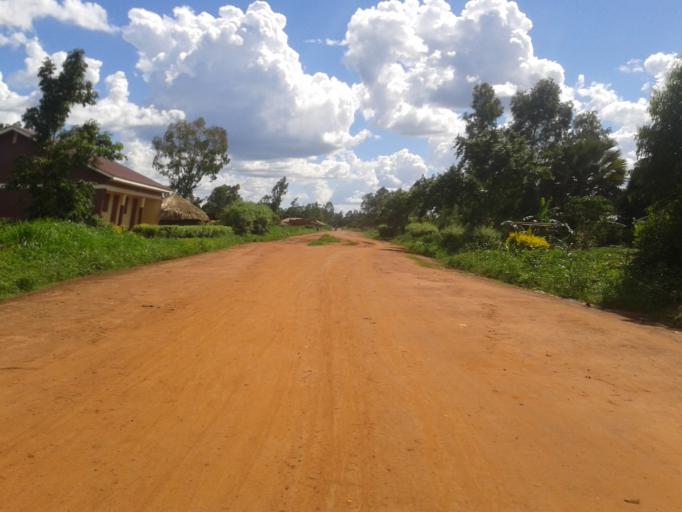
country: UG
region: Northern Region
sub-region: Gulu District
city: Gulu
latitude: 2.7586
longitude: 32.3161
